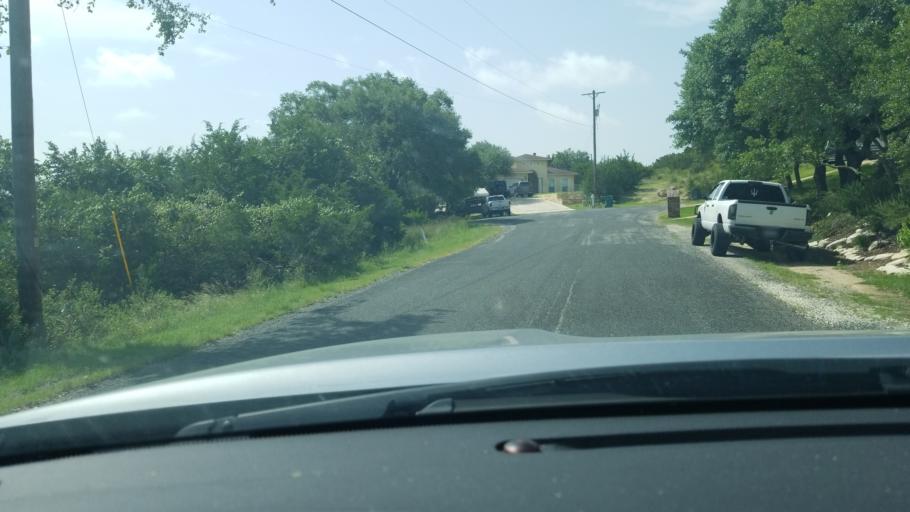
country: US
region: Texas
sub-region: Bexar County
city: Timberwood Park
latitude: 29.6888
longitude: -98.4909
